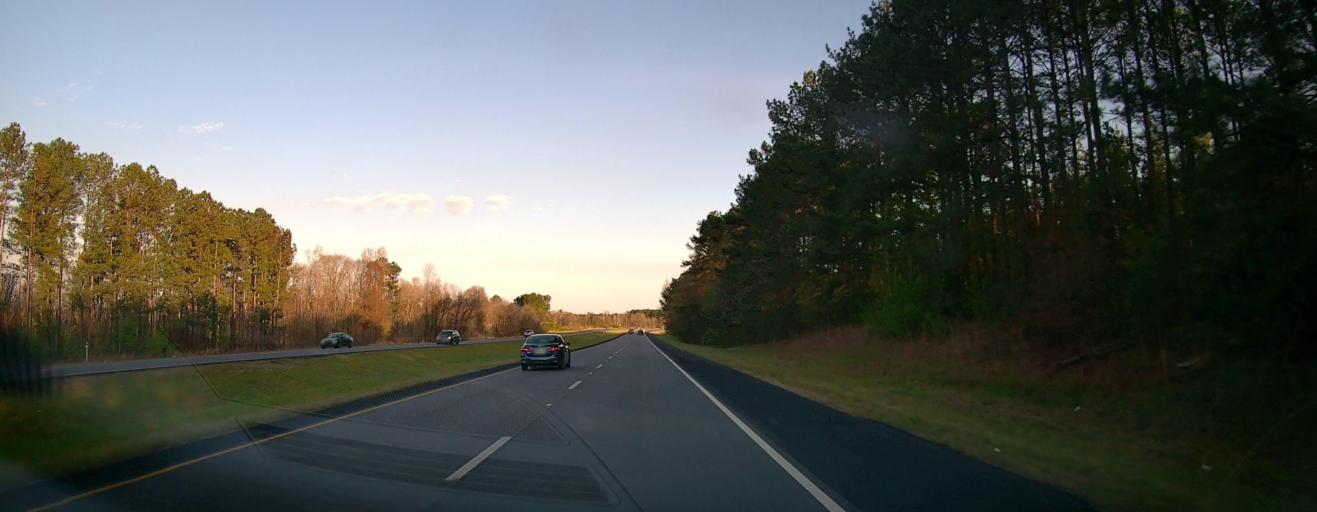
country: US
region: Alabama
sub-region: Talladega County
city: Childersburg
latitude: 33.3051
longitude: -86.3760
